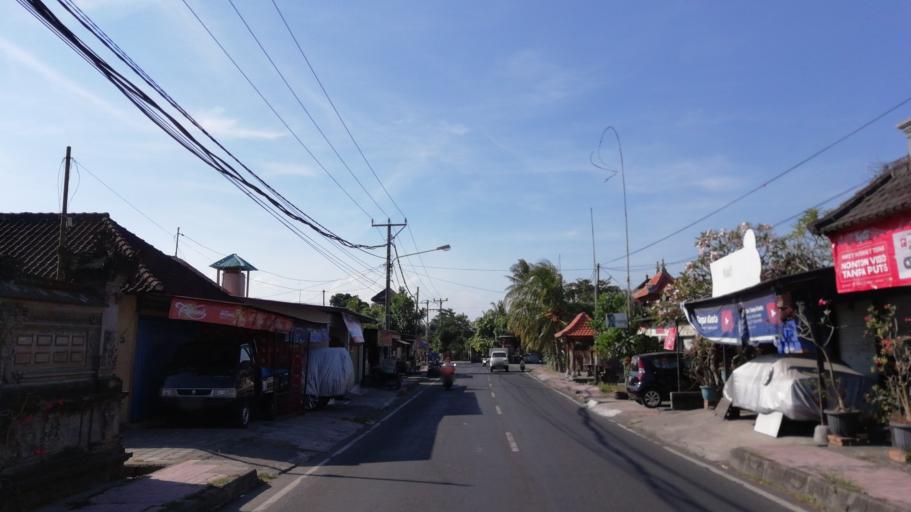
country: ID
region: Bali
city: Banjar Pasekan
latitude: -8.6262
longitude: 115.2843
